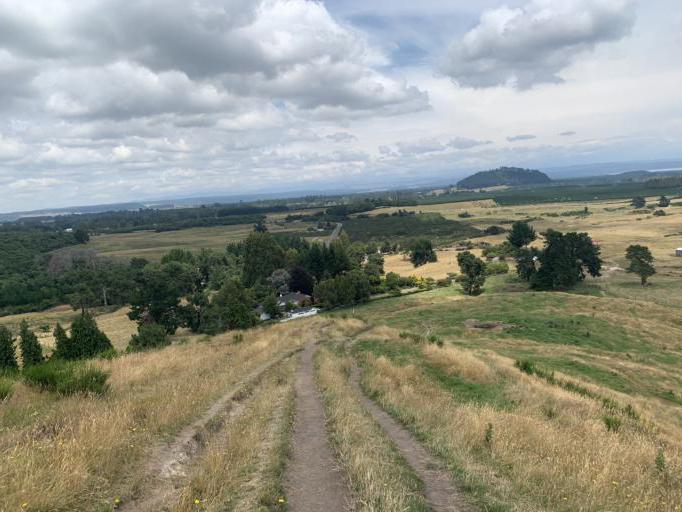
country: NZ
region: Waikato
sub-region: Taupo District
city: Taupo
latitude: -38.7016
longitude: 176.1422
